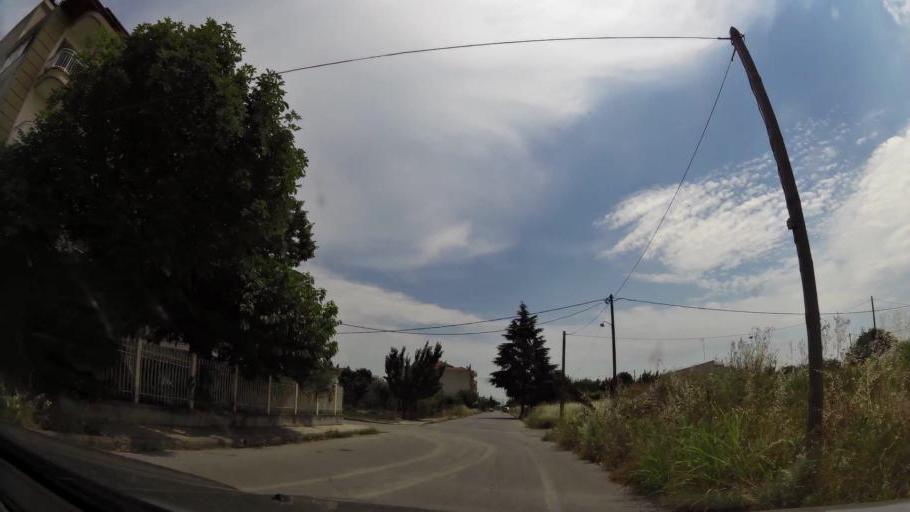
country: GR
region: Central Macedonia
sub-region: Nomos Pierias
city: Katerini
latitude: 40.2619
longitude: 22.5203
